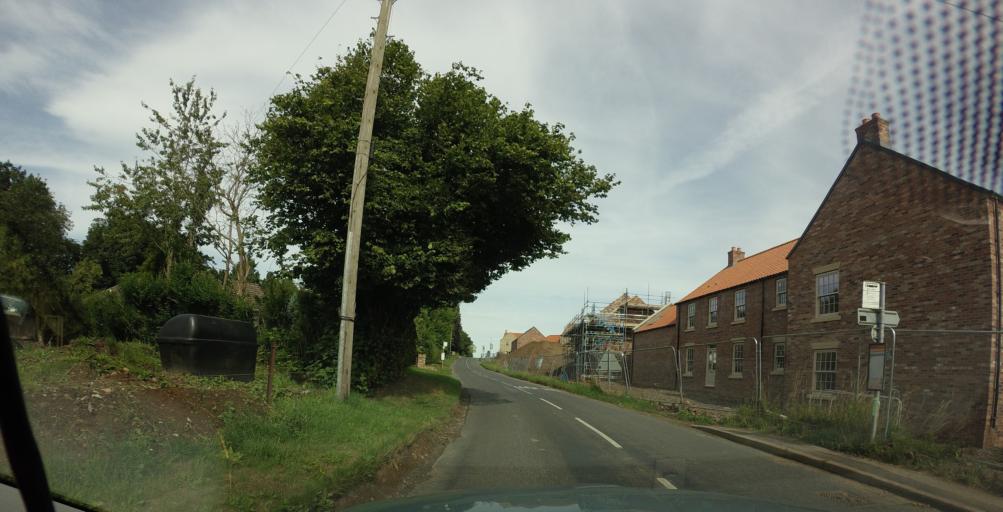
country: GB
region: England
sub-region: North Yorkshire
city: Ripon
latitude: 54.0920
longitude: -1.5036
